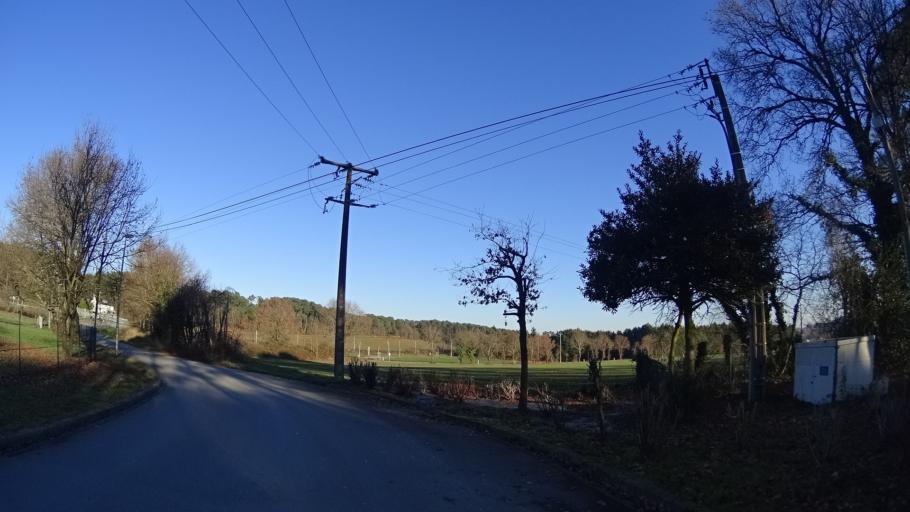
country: FR
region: Brittany
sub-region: Departement du Morbihan
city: Saint-Jacut-les-Pins
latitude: 47.6785
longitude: -2.1794
